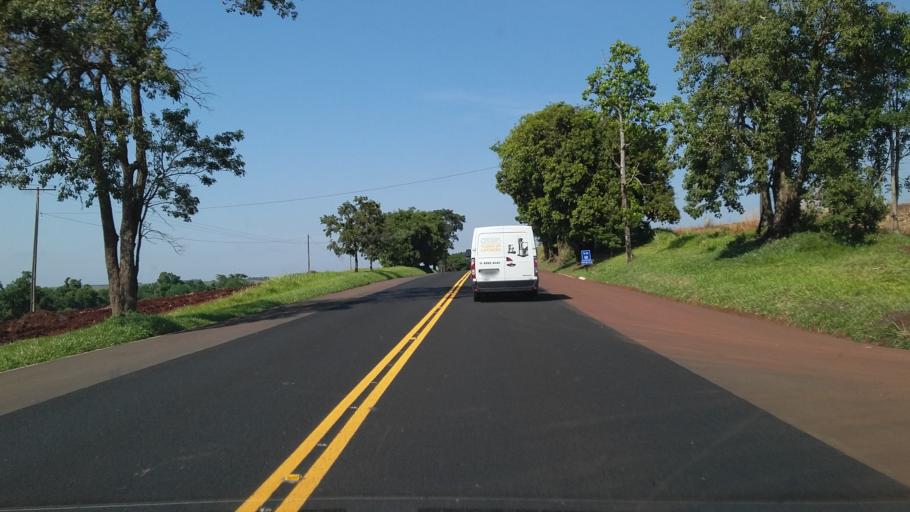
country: BR
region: Parana
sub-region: Bandeirantes
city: Bandeirantes
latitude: -23.1345
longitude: -50.4768
